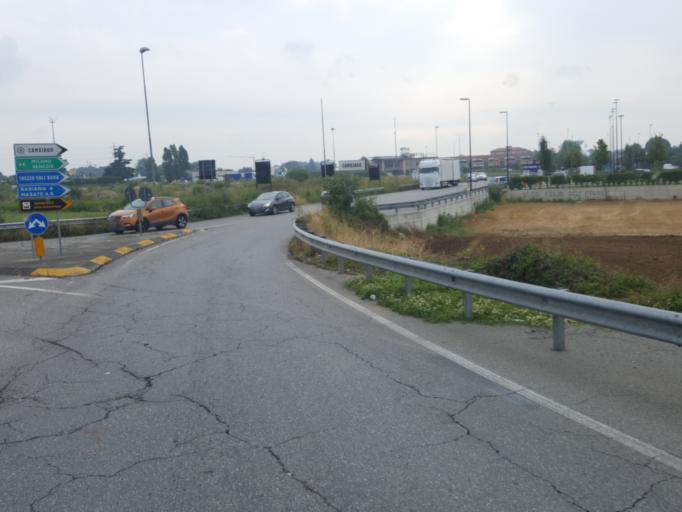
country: IT
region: Lombardy
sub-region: Provincia di Monza e Brianza
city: Cavenago di Brianza
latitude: 45.5748
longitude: 9.4138
